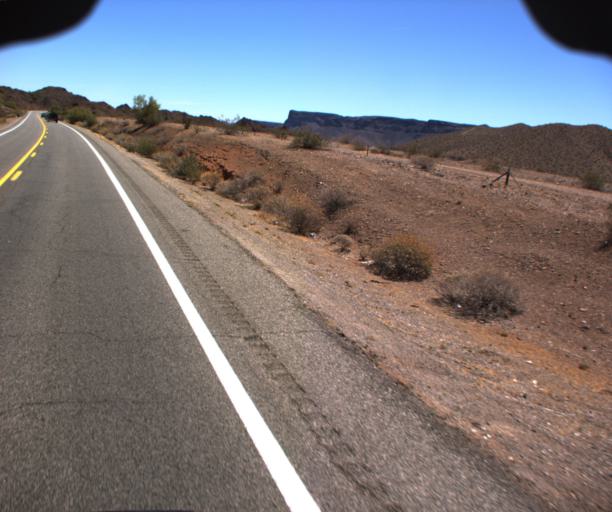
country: US
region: Arizona
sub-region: La Paz County
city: Cienega Springs
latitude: 34.3253
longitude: -114.1281
